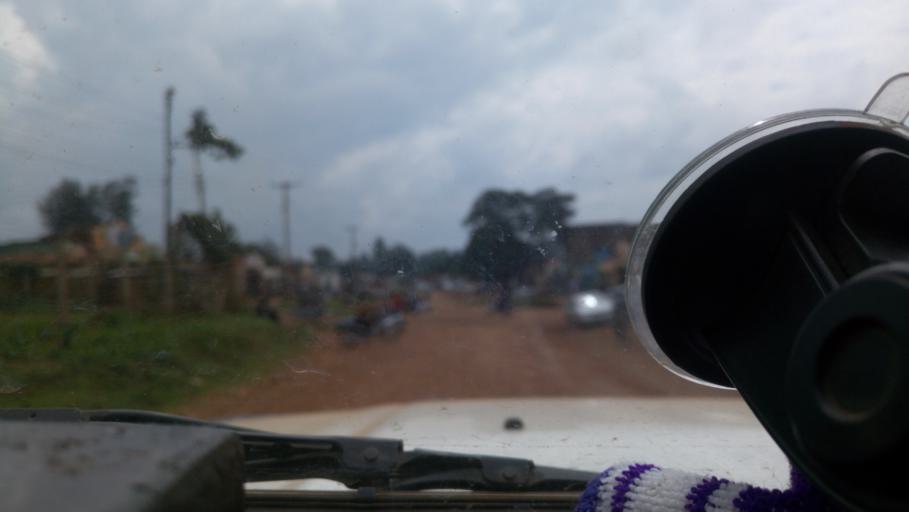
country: KE
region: Kericho
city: Litein
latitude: -0.6280
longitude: 35.1951
